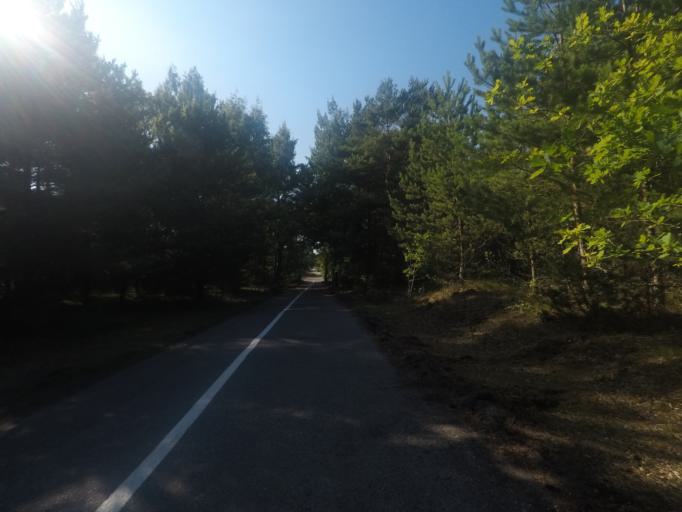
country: LT
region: Klaipedos apskritis
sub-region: Klaipeda
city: Klaipeda
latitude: 55.5490
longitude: 21.1028
